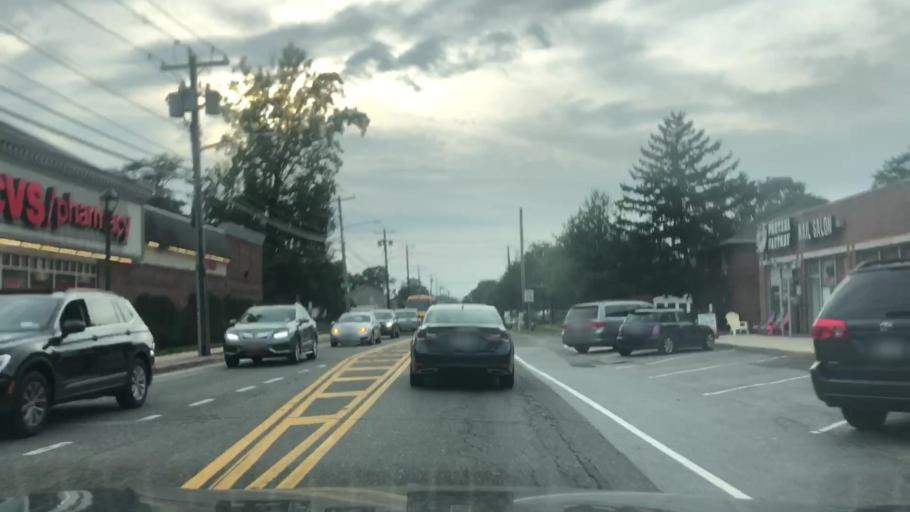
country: US
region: New York
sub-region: Nassau County
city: North Bellmore
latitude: 40.6915
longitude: -73.5341
